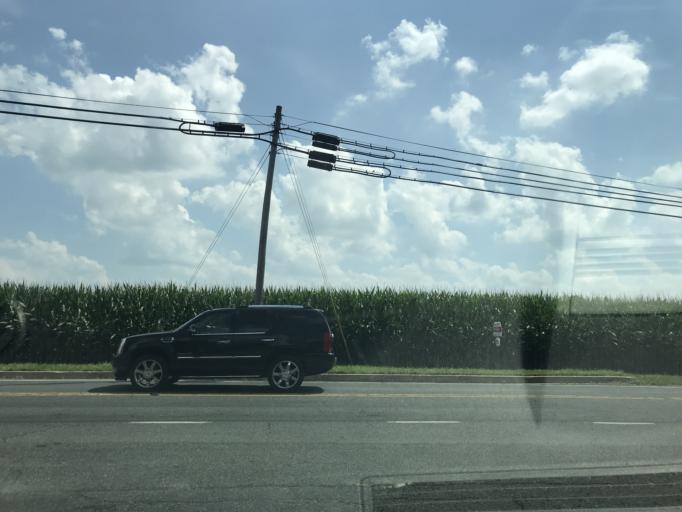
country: US
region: Maryland
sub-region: Carroll County
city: Hampstead
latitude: 39.6045
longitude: -76.8377
